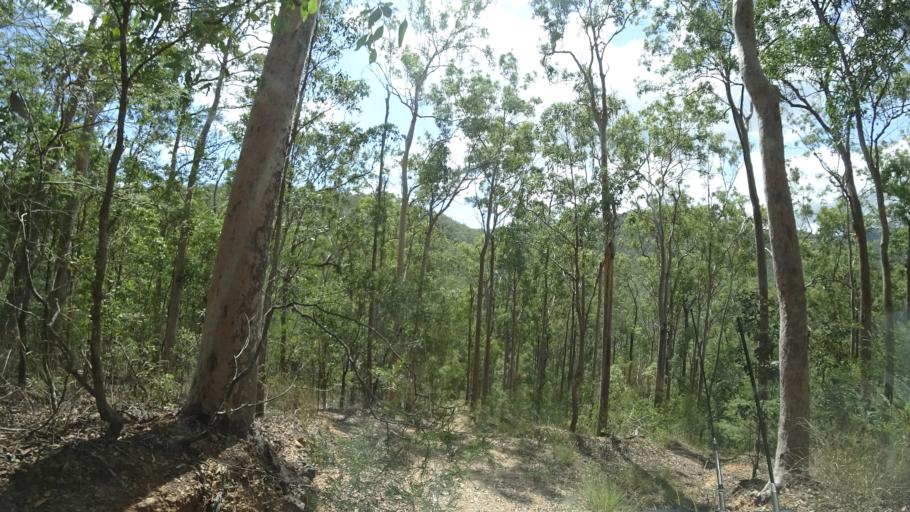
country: AU
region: Queensland
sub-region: Moreton Bay
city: Highvale
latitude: -27.3722
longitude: 152.7353
